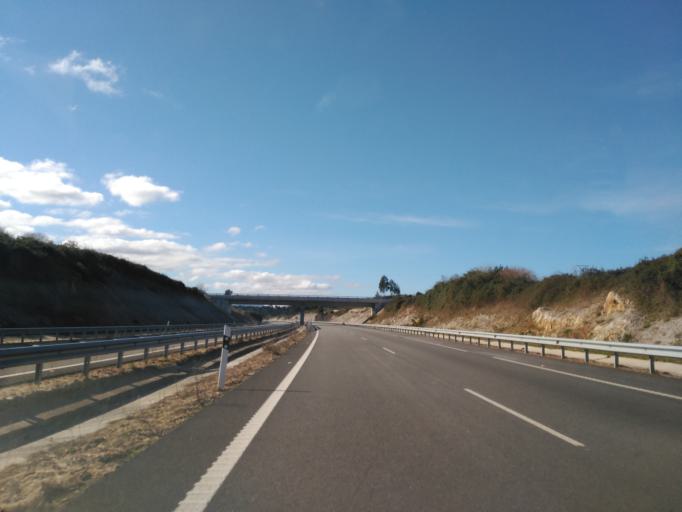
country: ES
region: Asturias
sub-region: Province of Asturias
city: Llanes
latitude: 43.4026
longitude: -4.6812
